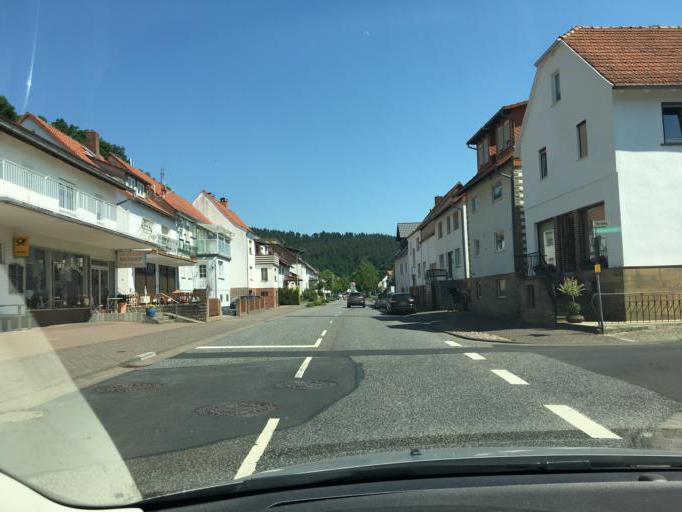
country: DE
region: Hesse
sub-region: Regierungsbezirk Kassel
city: Ronshausen
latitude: 50.9478
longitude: 9.8648
